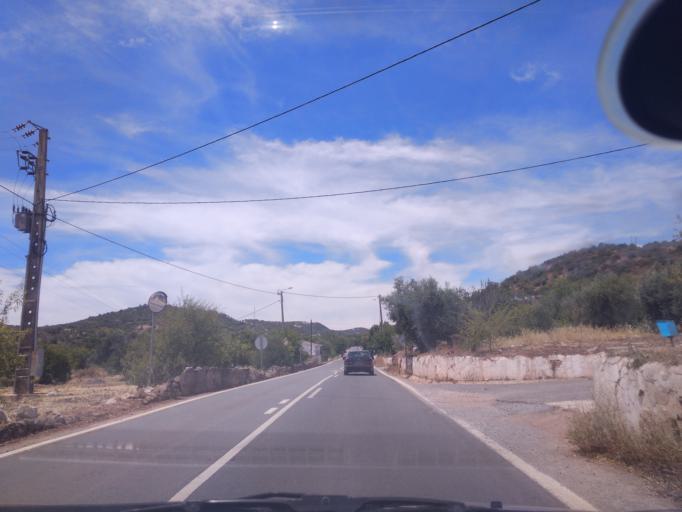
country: PT
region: Faro
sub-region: Olhao
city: Moncarapacho
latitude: 37.1521
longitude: -7.8044
